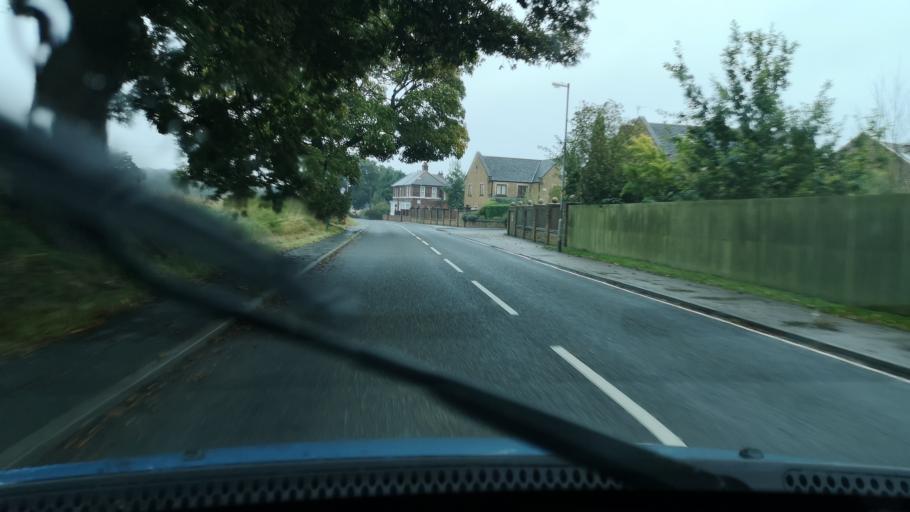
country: GB
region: England
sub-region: City and Borough of Wakefield
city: Featherstone
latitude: 53.6614
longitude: -1.3439
